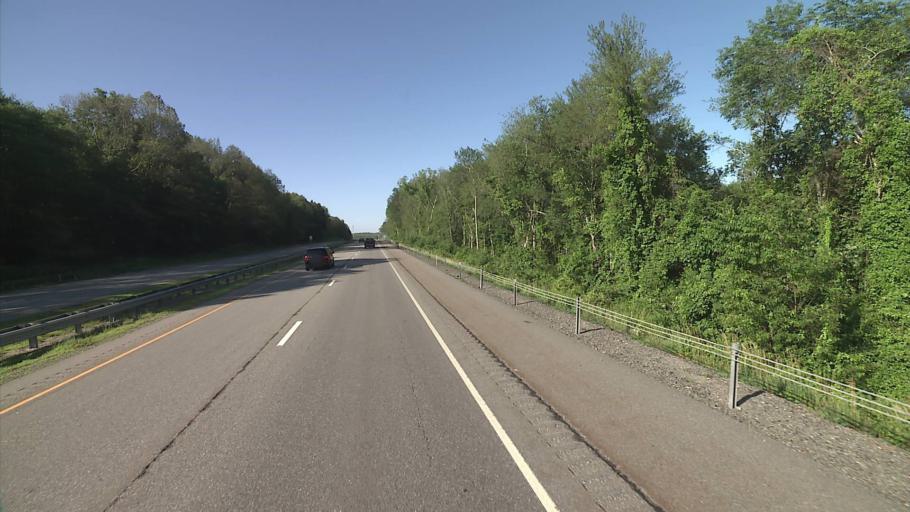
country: US
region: Connecticut
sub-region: Windham County
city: Moosup
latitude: 41.7277
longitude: -71.8902
